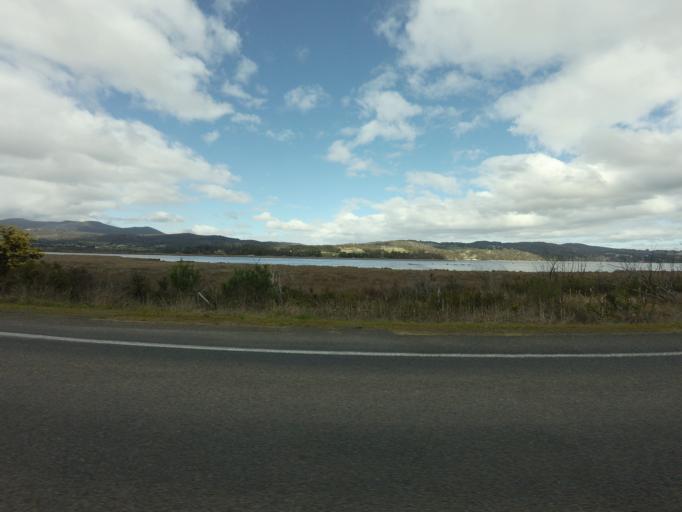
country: AU
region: Tasmania
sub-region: Huon Valley
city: Franklin
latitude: -43.1155
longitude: 146.9934
